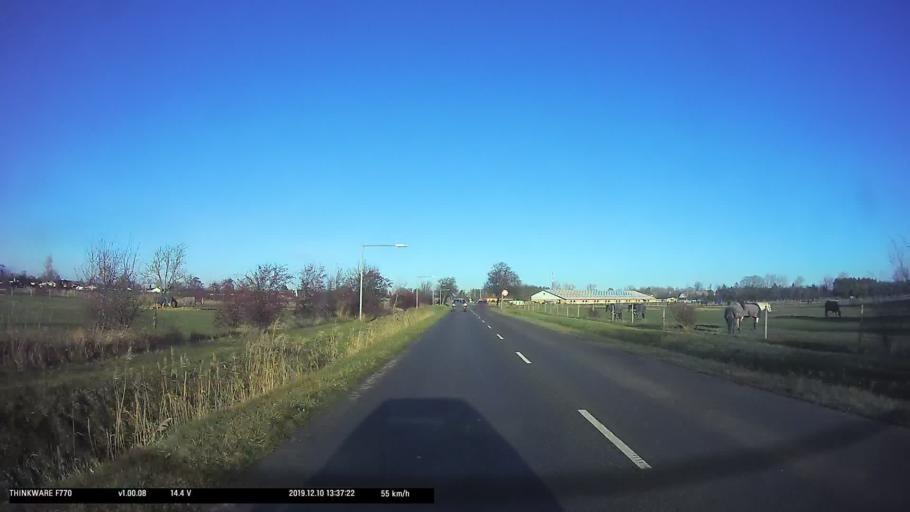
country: DK
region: Capital Region
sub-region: Tarnby Kommune
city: Tarnby
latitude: 55.5876
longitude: 12.5800
